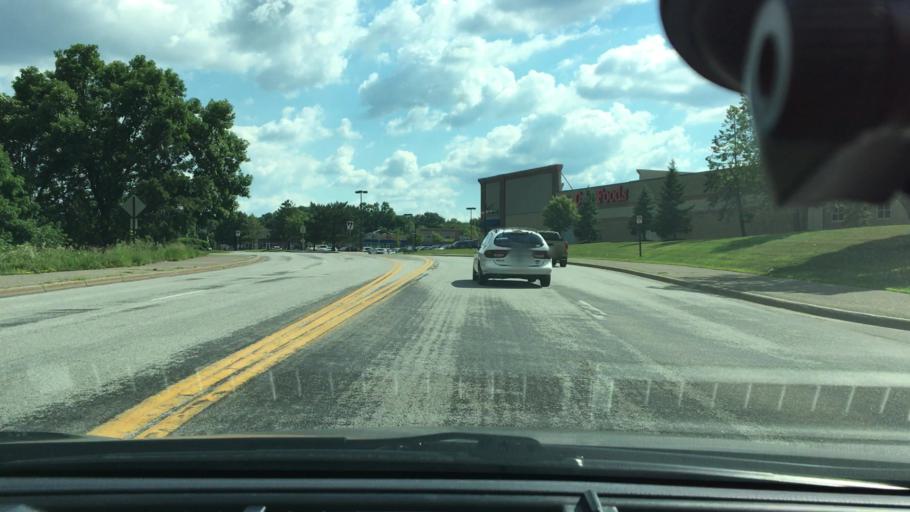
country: US
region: Minnesota
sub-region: Hennepin County
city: New Hope
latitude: 45.0360
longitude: -93.4083
